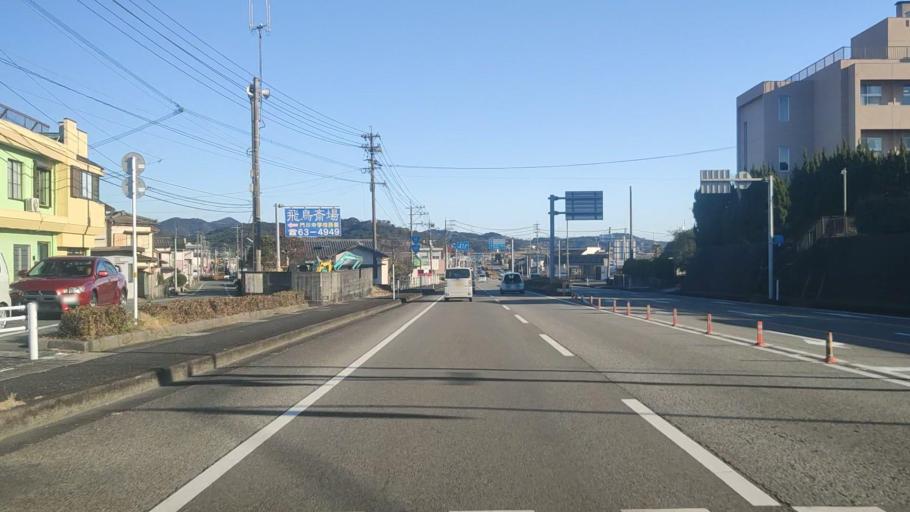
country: JP
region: Miyazaki
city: Nobeoka
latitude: 32.4731
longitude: 131.6519
